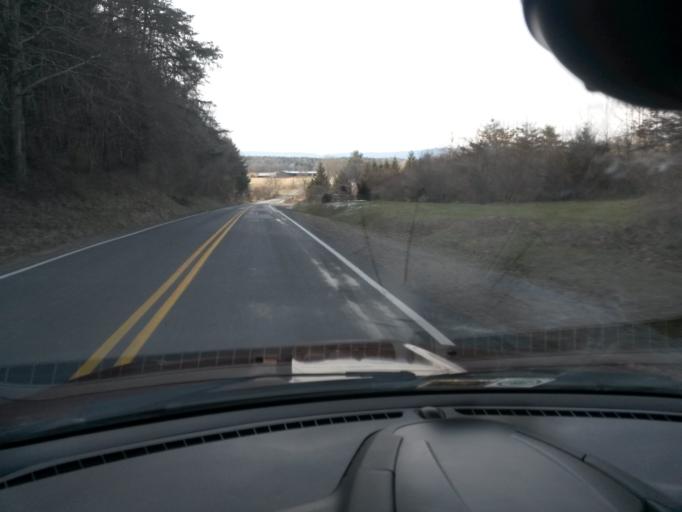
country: US
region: Virginia
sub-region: Bath County
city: Warm Springs
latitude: 37.9983
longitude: -79.5619
